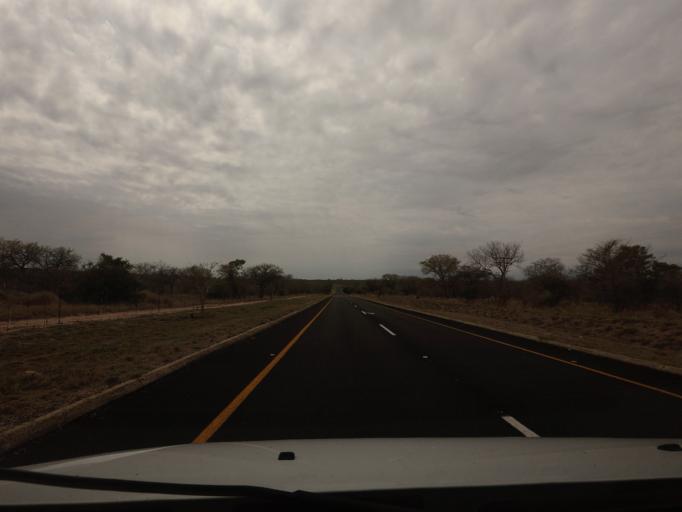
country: ZA
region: Limpopo
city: Thulamahashi
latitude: -24.5552
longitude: 31.2020
